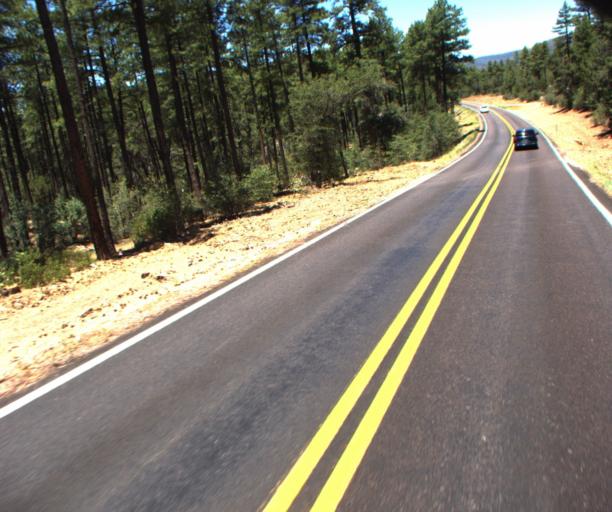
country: US
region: Arizona
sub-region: Gila County
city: Pine
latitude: 34.3653
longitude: -111.4325
